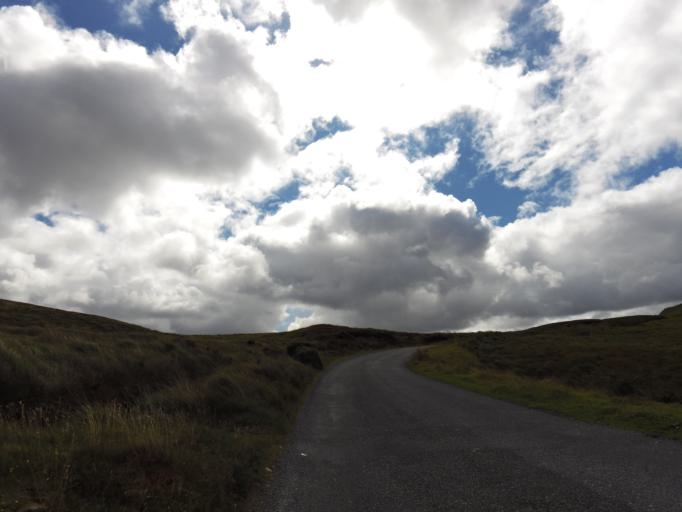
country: IE
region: Connaught
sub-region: County Galway
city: Oughterard
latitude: 53.3969
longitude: -9.3336
